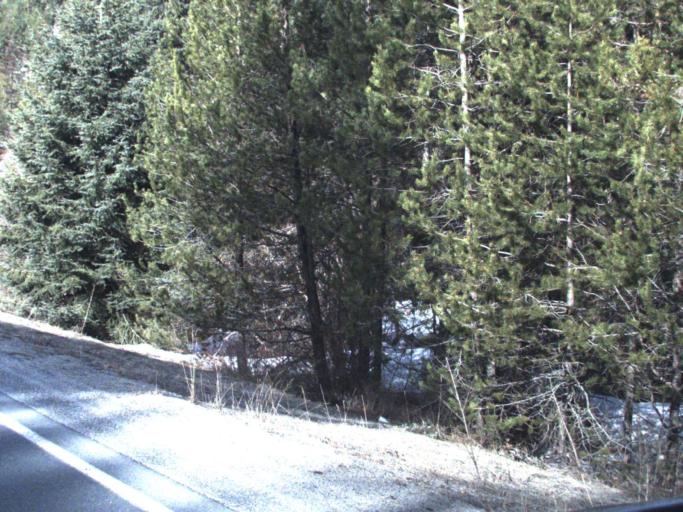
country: US
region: Washington
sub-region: Stevens County
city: Chewelah
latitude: 48.5343
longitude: -117.6115
